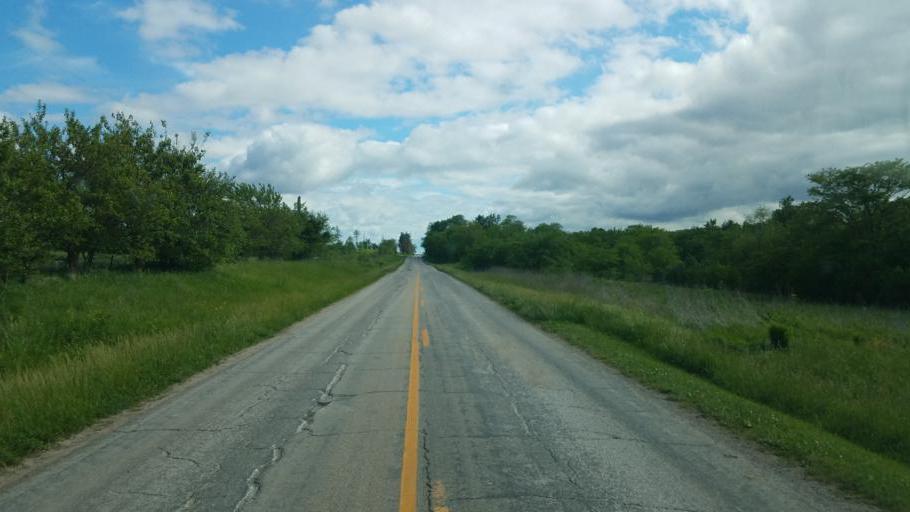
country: US
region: Missouri
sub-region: Mercer County
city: Princeton
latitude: 40.2563
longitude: -93.6757
